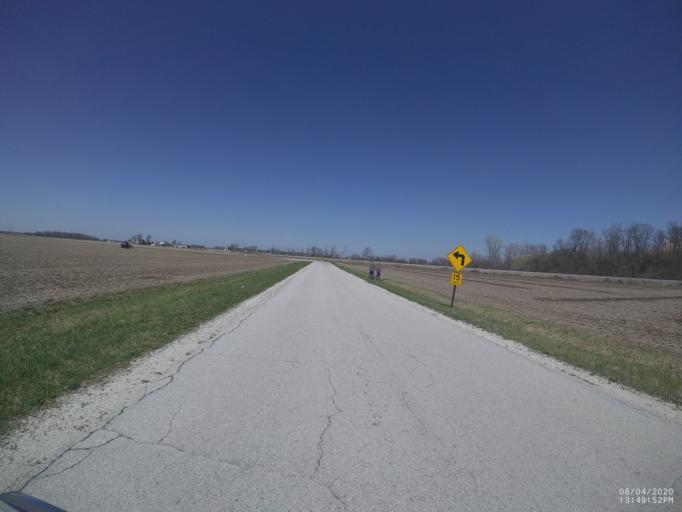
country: US
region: Ohio
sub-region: Sandusky County
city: Gibsonburg
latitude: 41.3253
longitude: -83.2869
